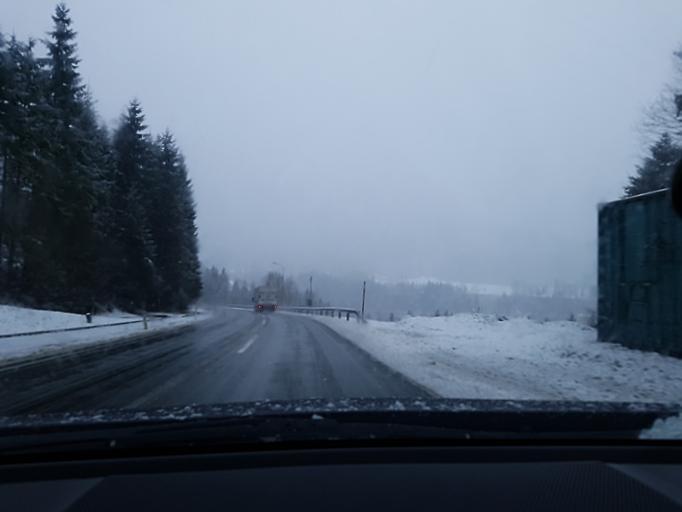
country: AT
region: Salzburg
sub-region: Politischer Bezirk Hallein
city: Scheffau am Tennengebirge
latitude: 47.5823
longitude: 13.2695
